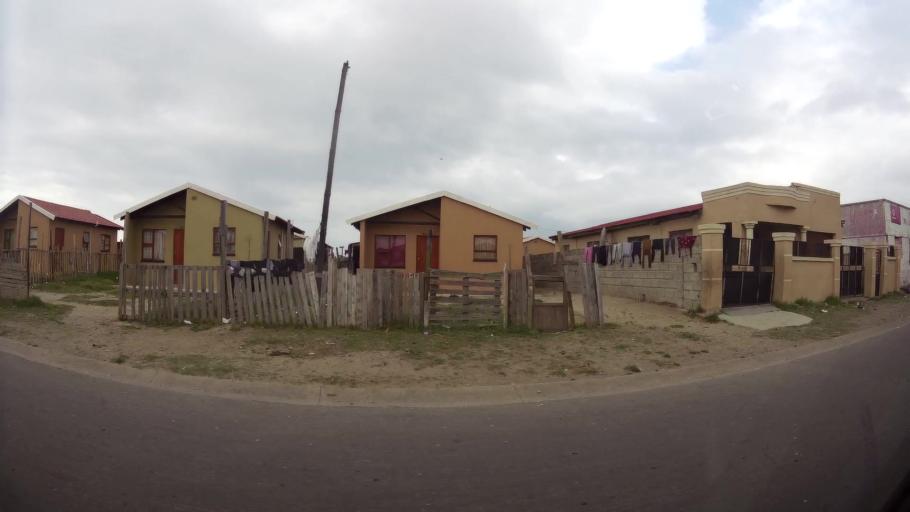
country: ZA
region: Eastern Cape
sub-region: Nelson Mandela Bay Metropolitan Municipality
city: Port Elizabeth
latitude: -33.8963
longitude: 25.6064
